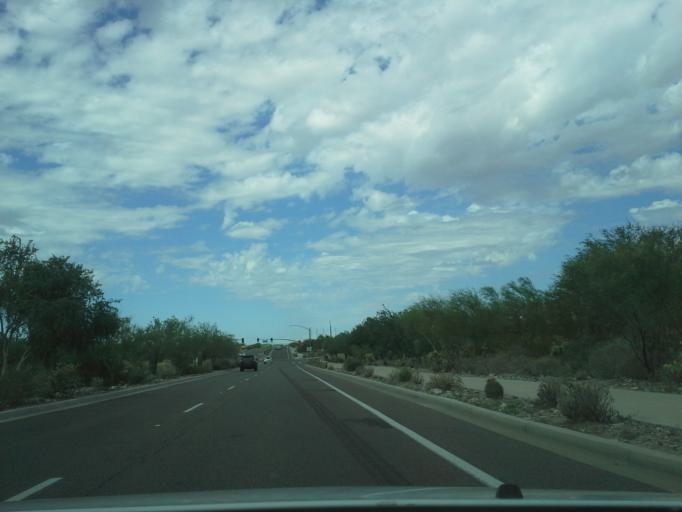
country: US
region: Arizona
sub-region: Maricopa County
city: Paradise Valley
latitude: 33.6402
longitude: -111.8676
